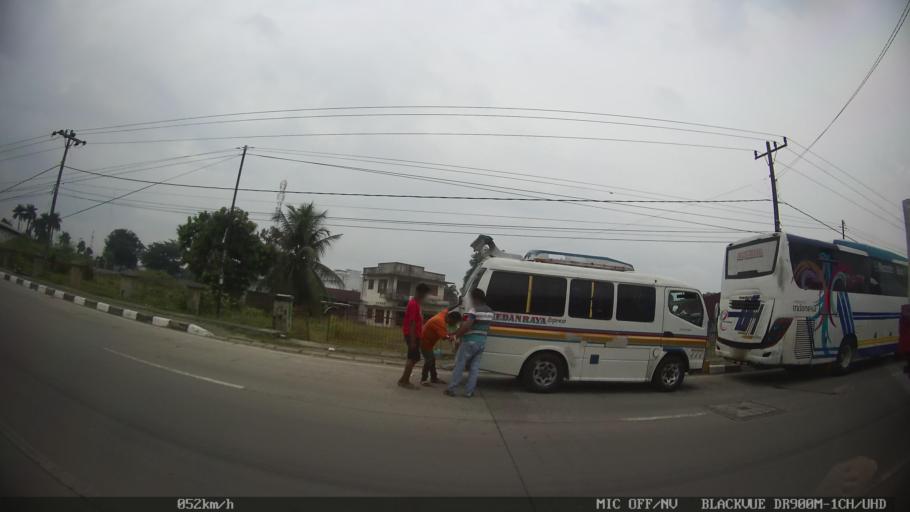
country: ID
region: North Sumatra
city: Deli Tua
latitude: 3.5400
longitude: 98.6999
